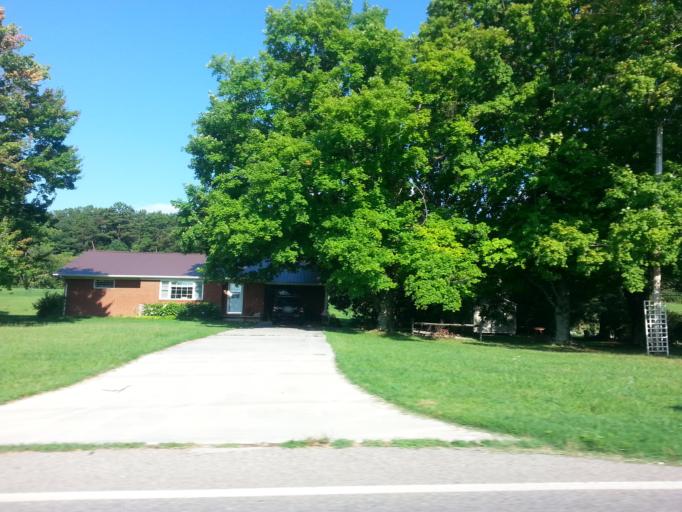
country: US
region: Tennessee
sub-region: Blount County
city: Louisville
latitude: 35.7803
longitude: -84.0247
